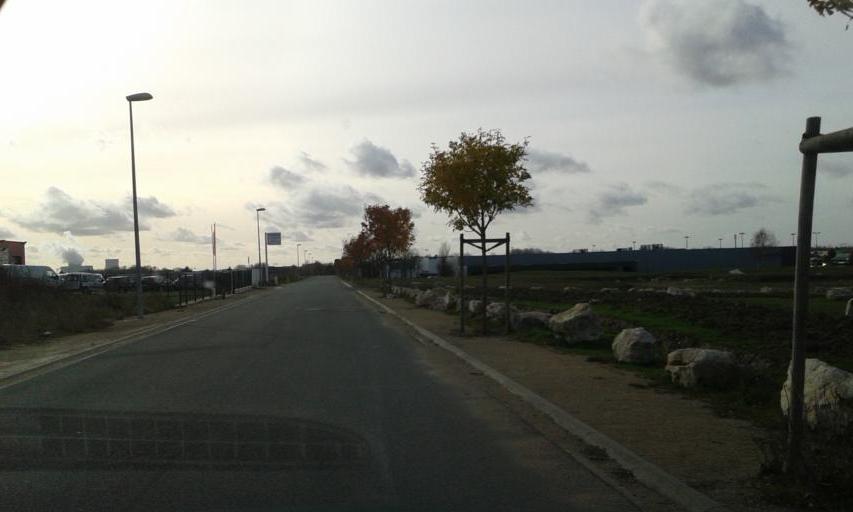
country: FR
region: Centre
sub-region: Departement du Loiret
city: Tavers
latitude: 47.7676
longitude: 1.6176
